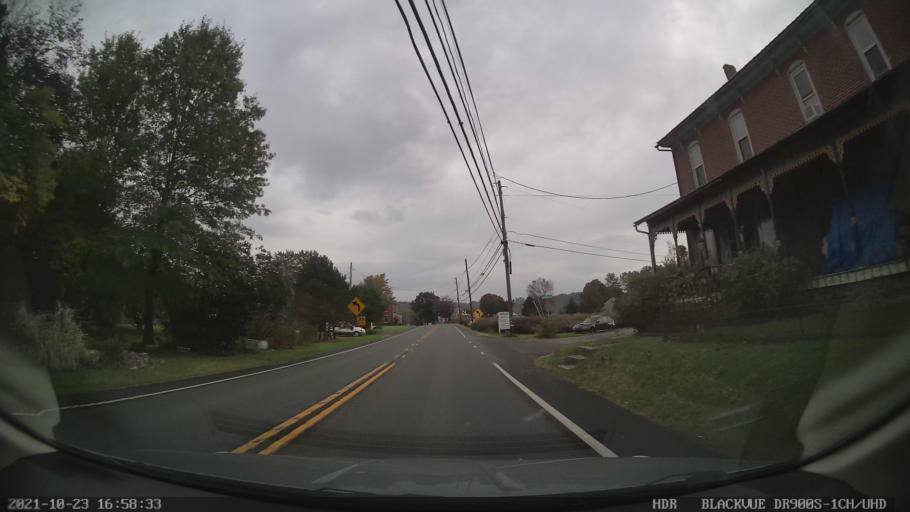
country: US
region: Pennsylvania
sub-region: Berks County
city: Bally
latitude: 40.4347
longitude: -75.5461
